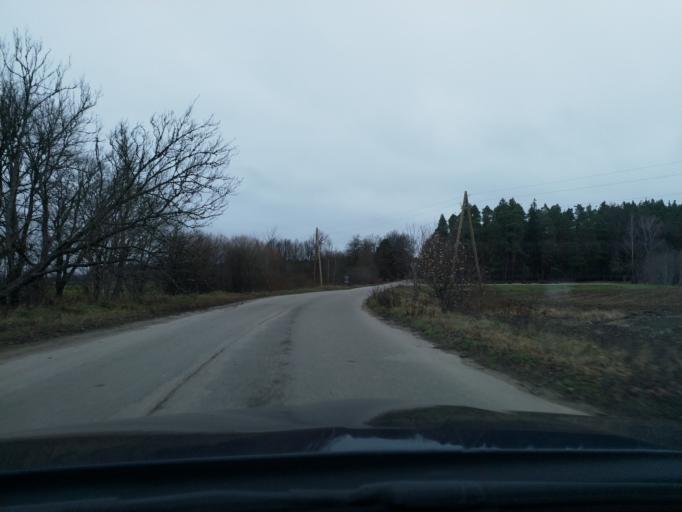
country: LV
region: Ventspils Rajons
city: Piltene
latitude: 57.1190
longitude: 21.8113
